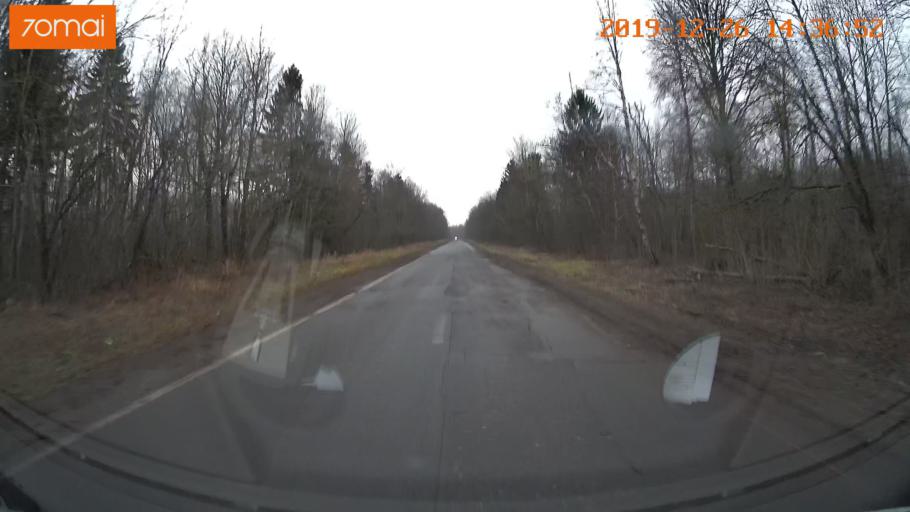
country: RU
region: Jaroslavl
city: Poshekhon'ye
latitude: 58.4076
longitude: 38.9745
